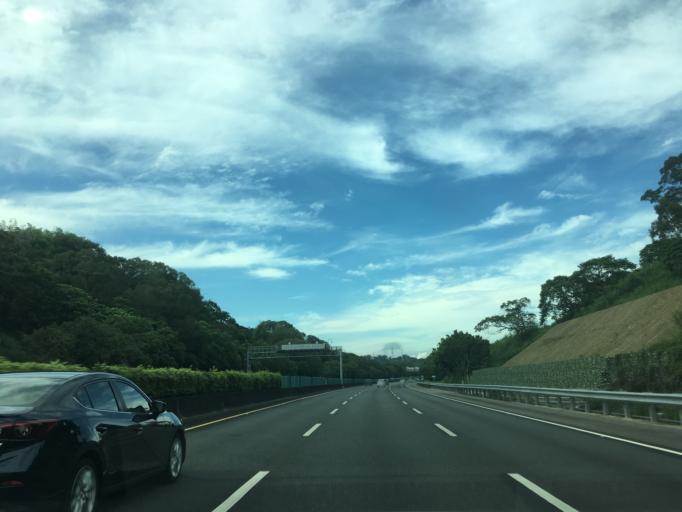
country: TW
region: Taiwan
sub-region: Chiayi
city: Jiayi Shi
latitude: 23.5276
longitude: 120.4864
